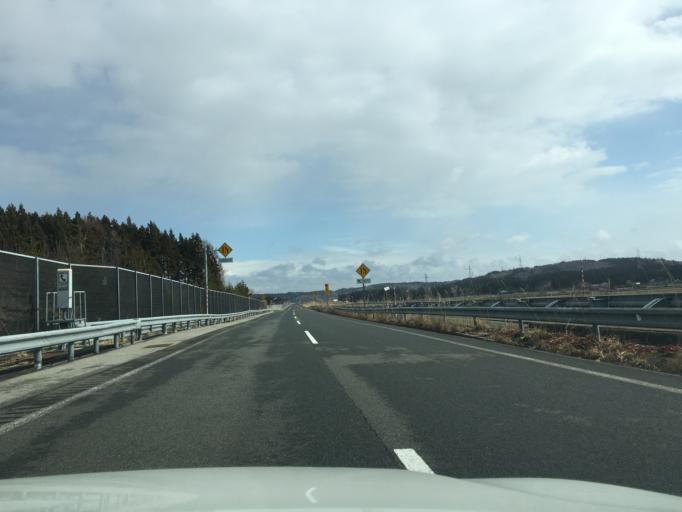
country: JP
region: Akita
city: Akita
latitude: 39.6138
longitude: 140.1422
